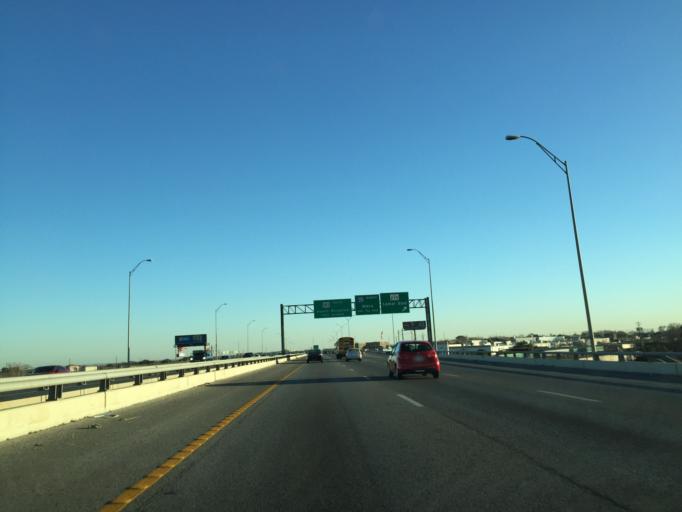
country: US
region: Texas
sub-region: Travis County
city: Austin
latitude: 30.3555
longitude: -97.7153
